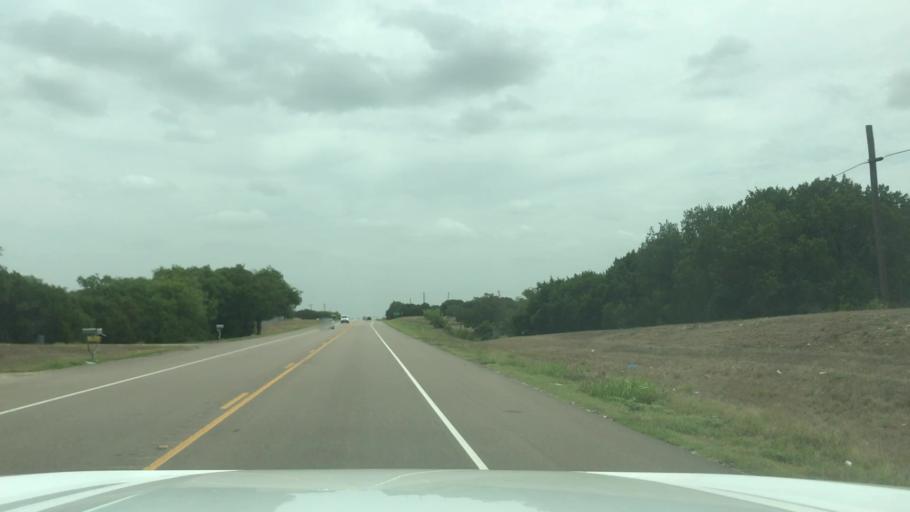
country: US
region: Texas
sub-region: McLennan County
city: Woodway
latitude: 31.5909
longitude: -97.3313
